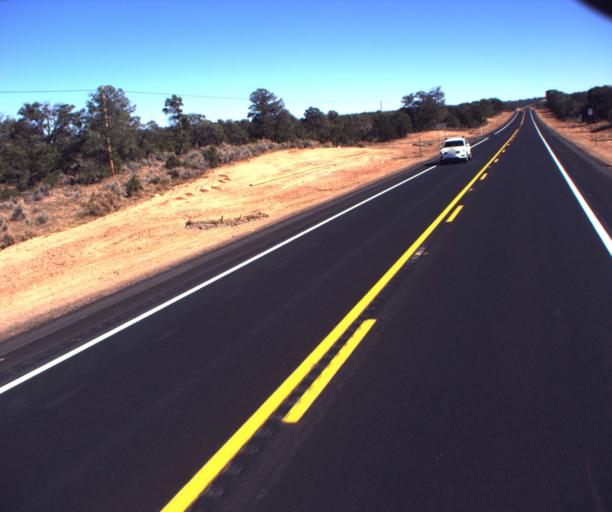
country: US
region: Arizona
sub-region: Apache County
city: Ganado
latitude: 35.7193
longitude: -109.3661
